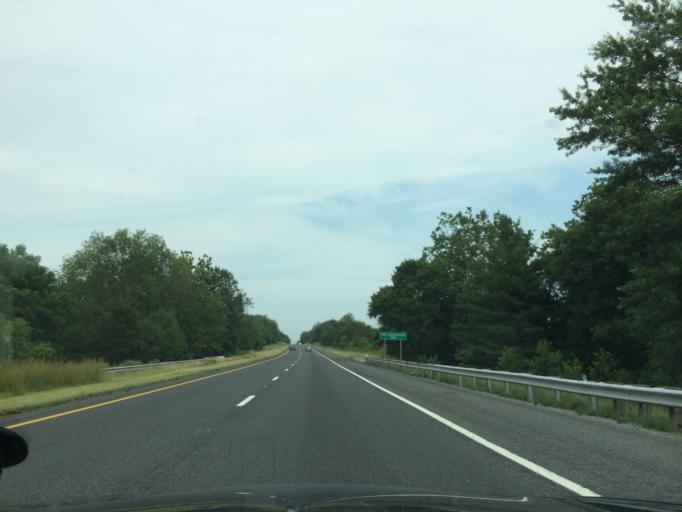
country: US
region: Maryland
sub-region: Washington County
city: Wilson-Conococheague
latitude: 39.6512
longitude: -77.8992
